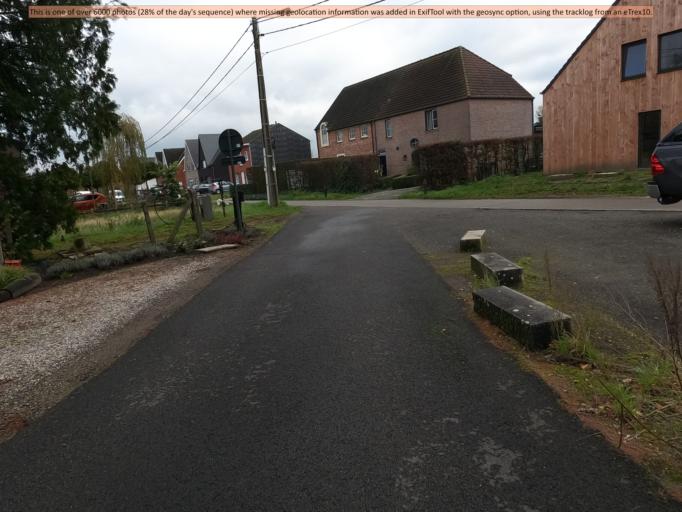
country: BE
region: Flanders
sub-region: Provincie Antwerpen
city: Nijlen
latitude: 51.1419
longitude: 4.6878
